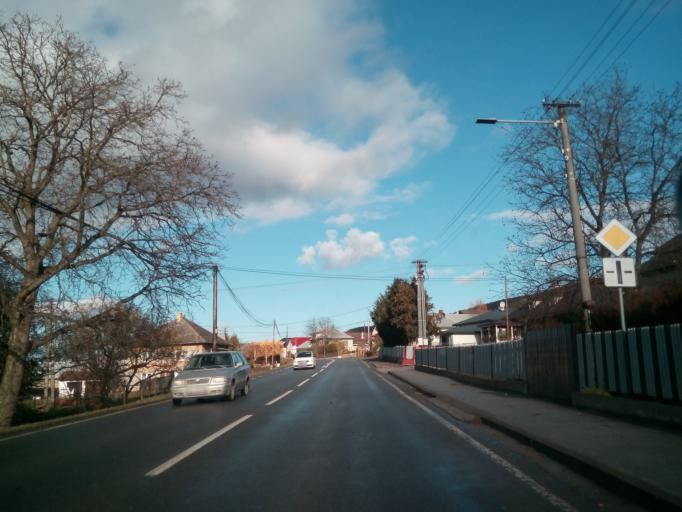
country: SK
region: Presovsky
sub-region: Okres Bardejov
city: Bardejov
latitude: 49.2154
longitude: 21.2960
